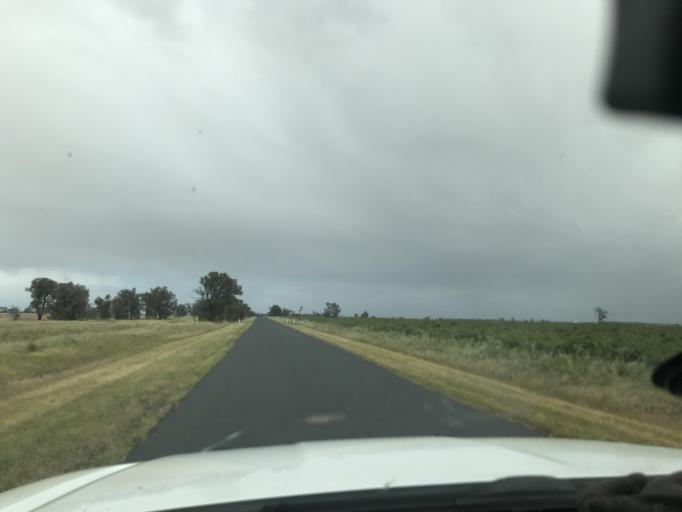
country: AU
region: South Australia
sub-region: Tatiara
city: Bordertown
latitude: -36.4068
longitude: 141.1912
